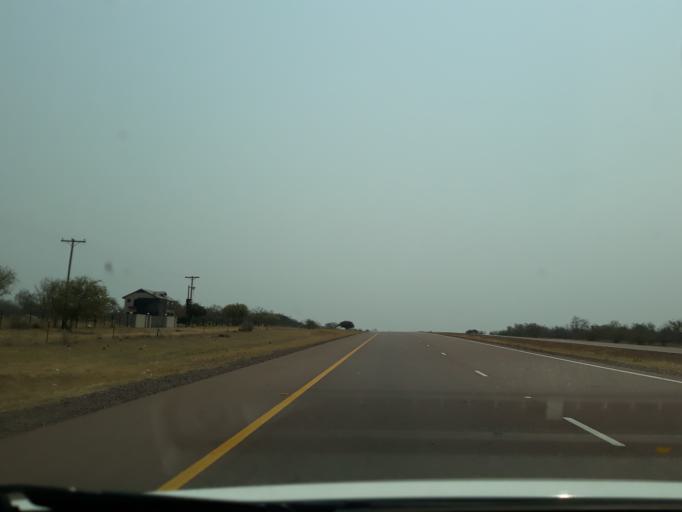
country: BW
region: Kgatleng
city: Bokaa
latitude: -24.3786
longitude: 26.0626
